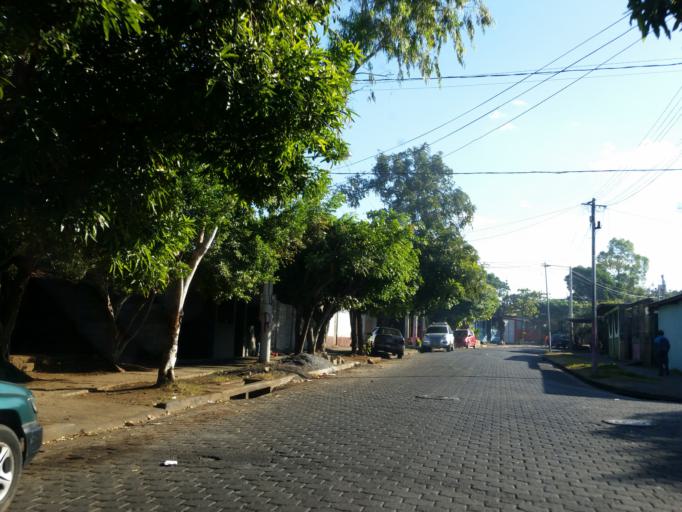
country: NI
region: Managua
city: Managua
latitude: 12.1228
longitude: -86.2937
